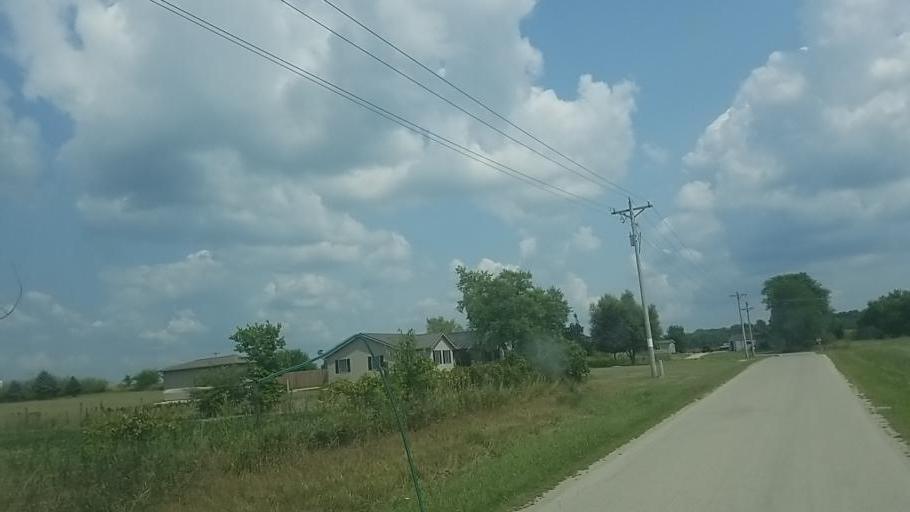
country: US
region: Ohio
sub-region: Wyandot County
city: Upper Sandusky
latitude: 40.9210
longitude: -83.1332
